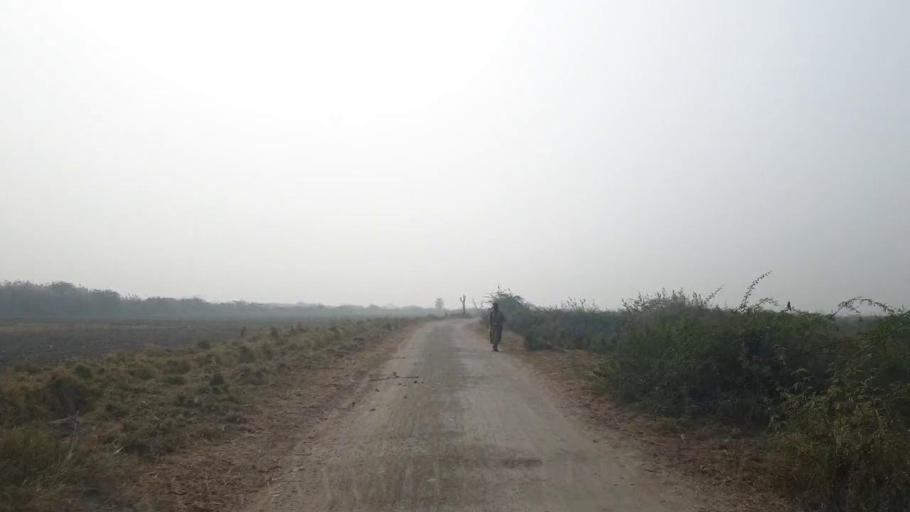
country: PK
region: Sindh
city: Bhit Shah
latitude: 25.7934
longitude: 68.5593
